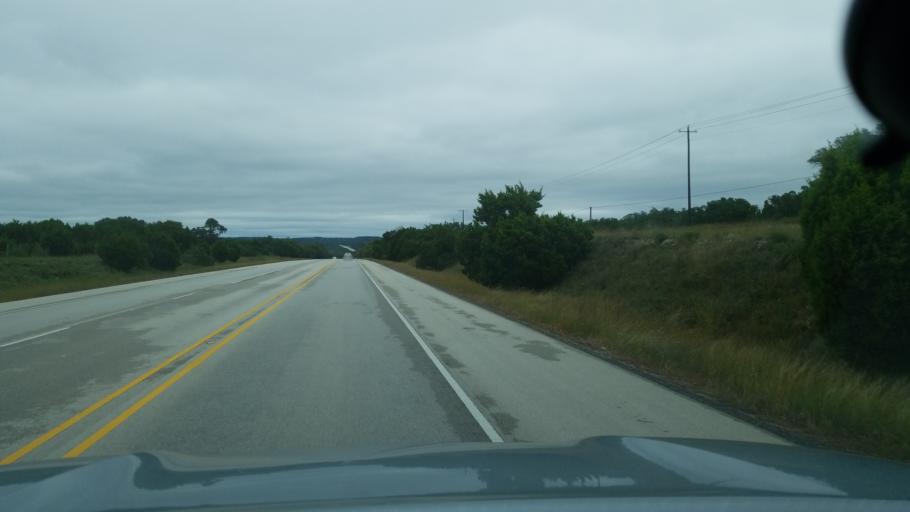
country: US
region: Texas
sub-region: Blanco County
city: Blanco
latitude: 29.9838
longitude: -98.4088
